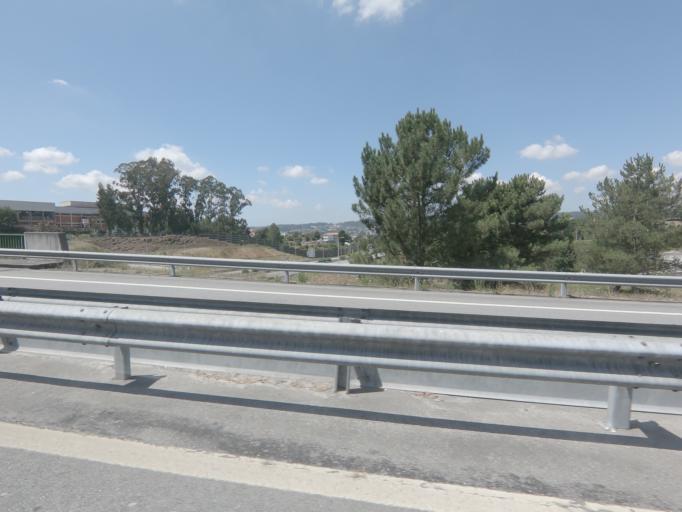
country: PT
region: Porto
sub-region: Paredes
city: Paredes
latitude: 41.2021
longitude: -8.3087
